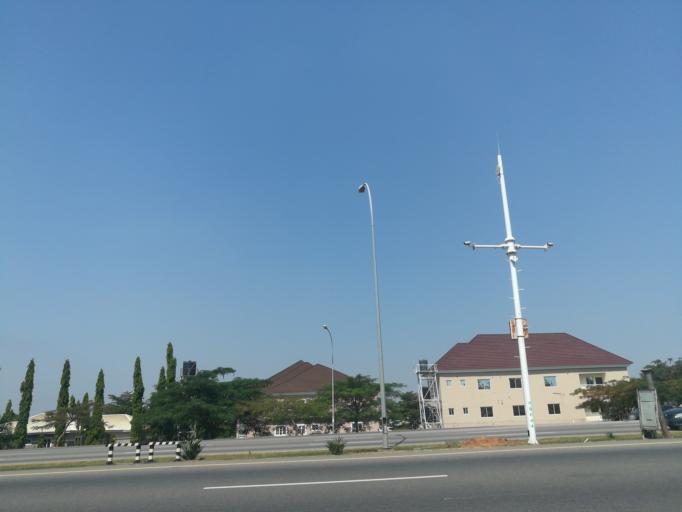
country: NG
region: Abuja Federal Capital Territory
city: Abuja
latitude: 9.0744
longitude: 7.4536
